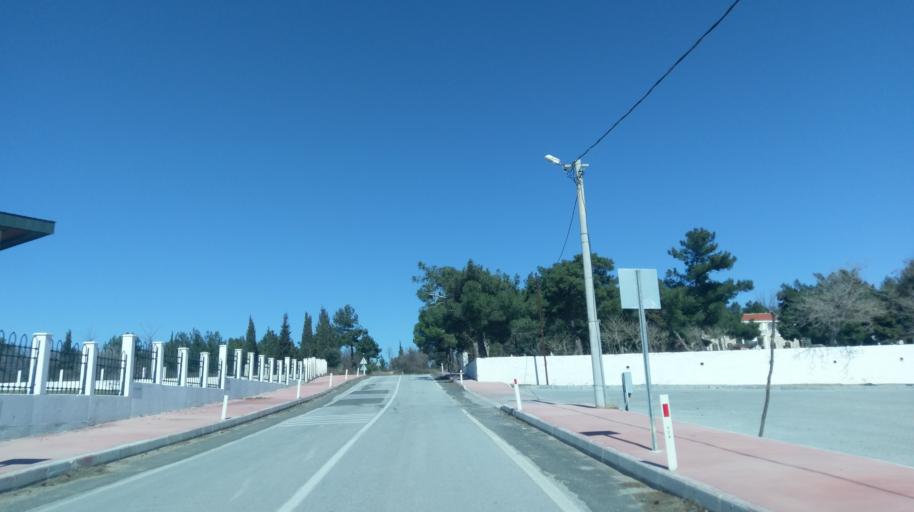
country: TR
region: Canakkale
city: Intepe
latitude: 40.0971
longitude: 26.2264
